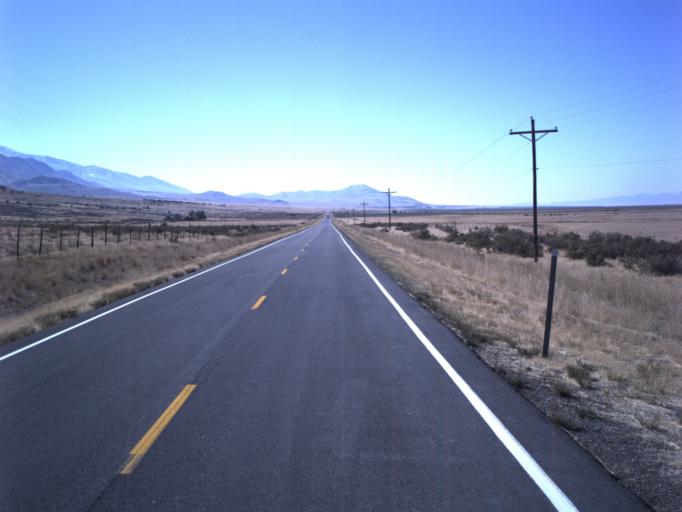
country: US
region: Utah
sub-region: Tooele County
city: Grantsville
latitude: 40.6949
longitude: -112.6673
